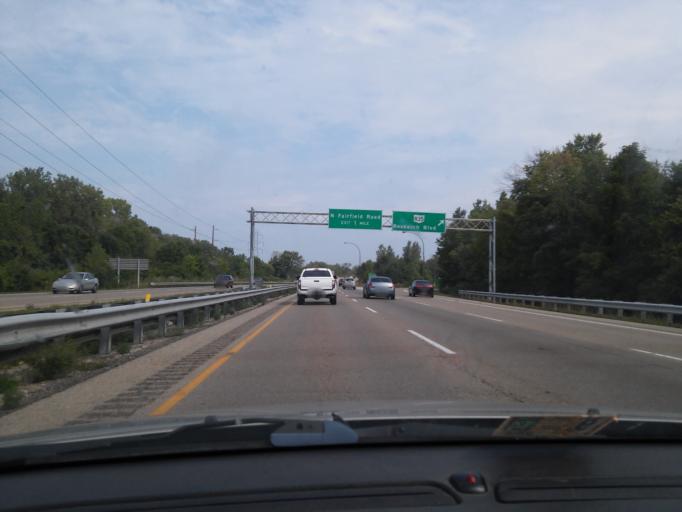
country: US
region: Ohio
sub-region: Greene County
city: Beavercreek
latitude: 39.7296
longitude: -84.0732
